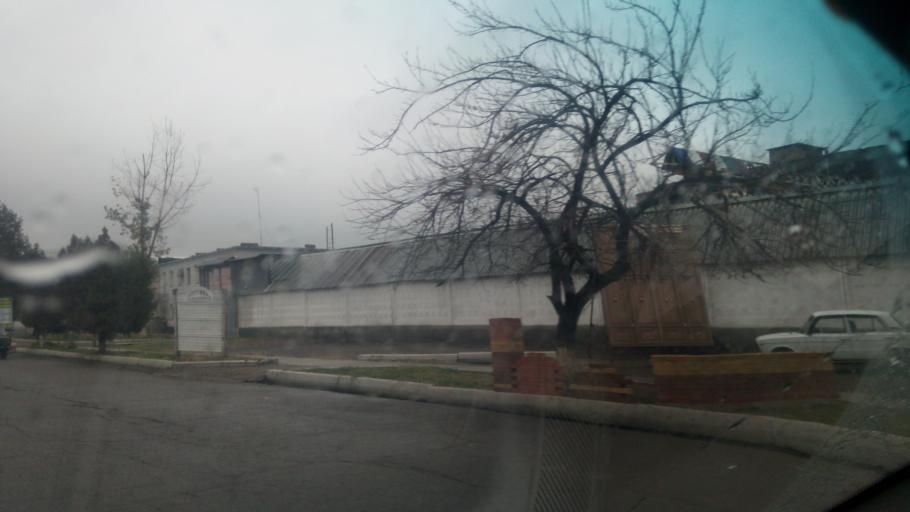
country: UZ
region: Toshkent Shahri
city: Bektemir
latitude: 41.2489
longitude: 69.3521
